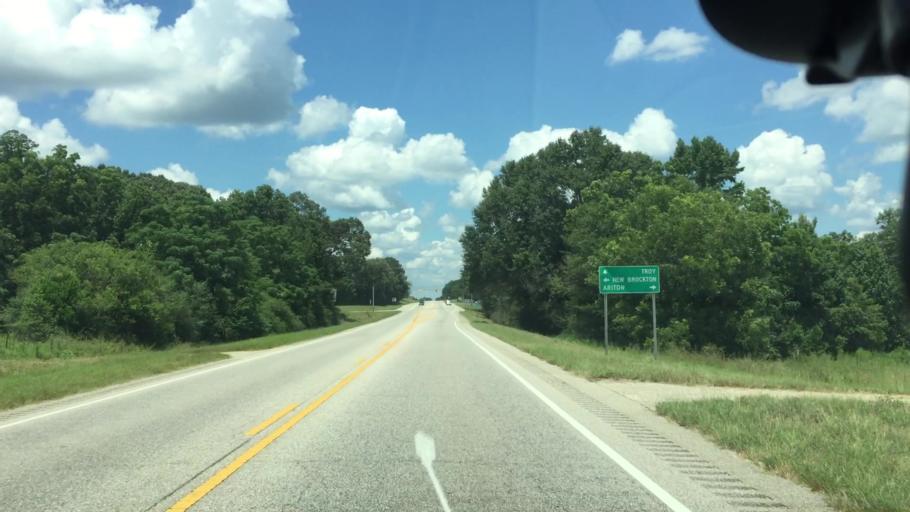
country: US
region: Alabama
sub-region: Coffee County
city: New Brockton
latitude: 31.4235
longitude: -85.8874
